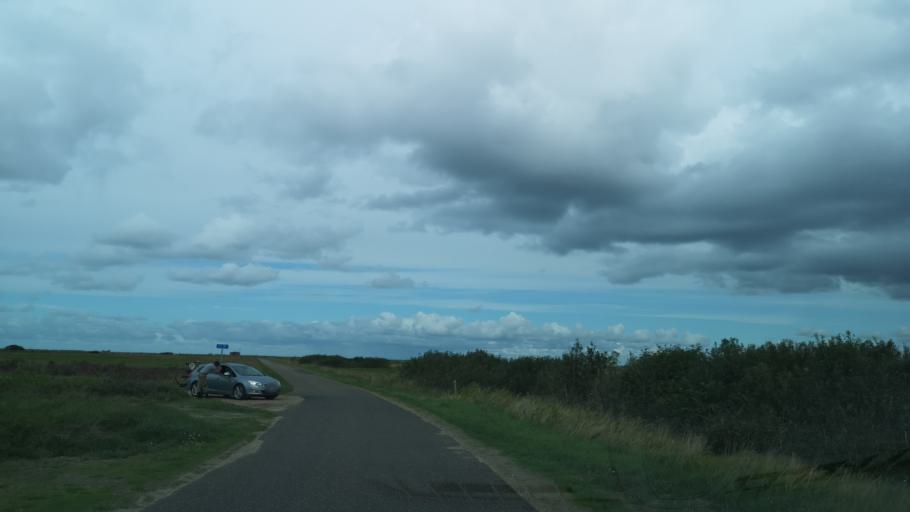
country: DK
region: Central Jutland
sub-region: Ringkobing-Skjern Kommune
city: Hvide Sande
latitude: 55.8520
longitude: 8.2191
